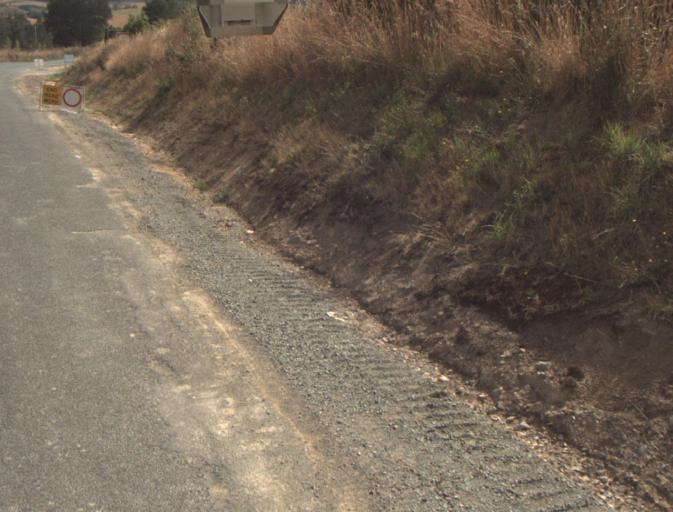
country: AU
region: Tasmania
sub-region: Launceston
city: Mayfield
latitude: -41.2597
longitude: 147.2074
